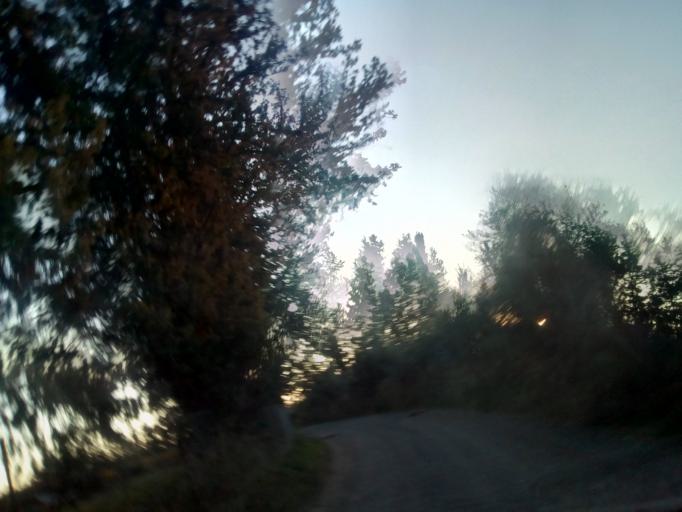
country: CY
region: Limassol
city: Ypsonas
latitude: 34.6573
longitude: 32.9783
